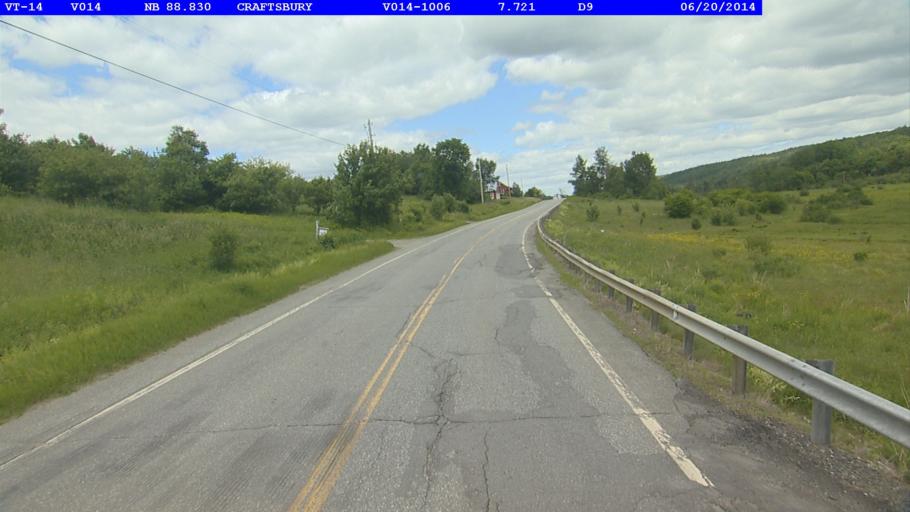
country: US
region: Vermont
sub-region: Caledonia County
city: Hardwick
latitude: 44.7000
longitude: -72.3943
